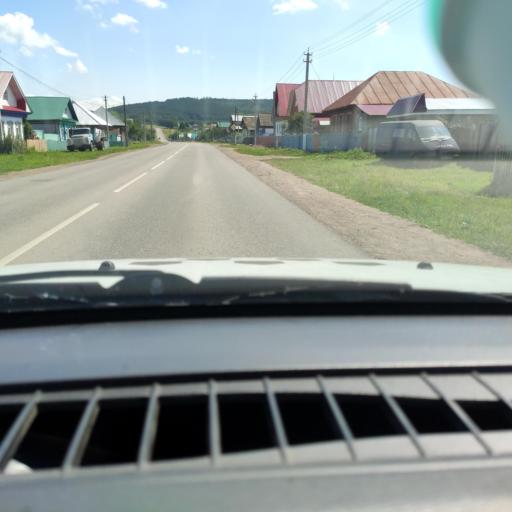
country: RU
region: Bashkortostan
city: Mesyagutovo
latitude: 55.5268
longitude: 58.2798
